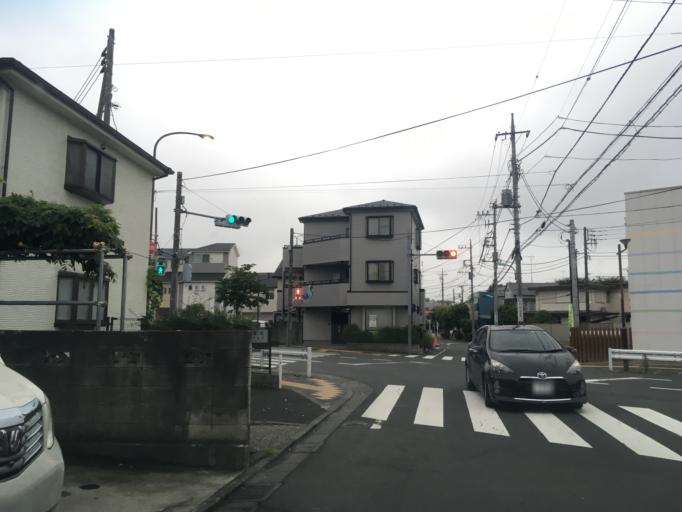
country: JP
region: Tokyo
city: Chofugaoka
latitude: 35.6483
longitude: 139.5333
